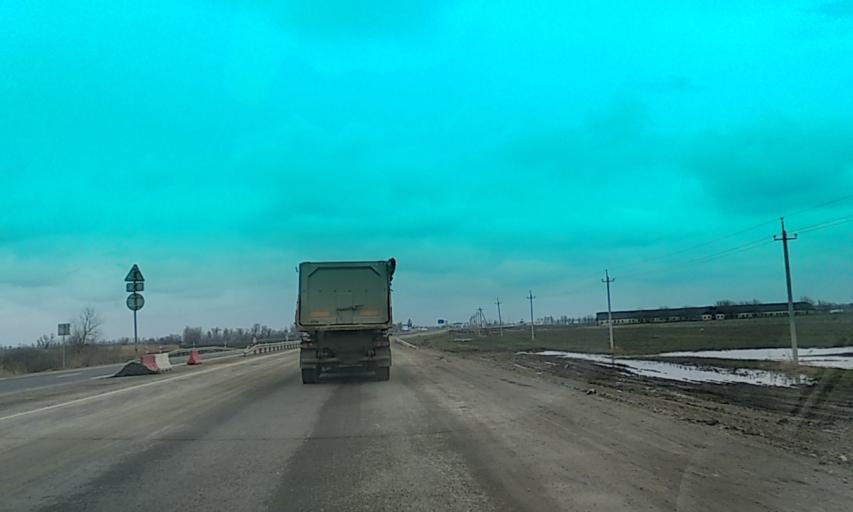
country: RU
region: Krasnodarskiy
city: Velikovechnoye
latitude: 44.9897
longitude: 39.7156
